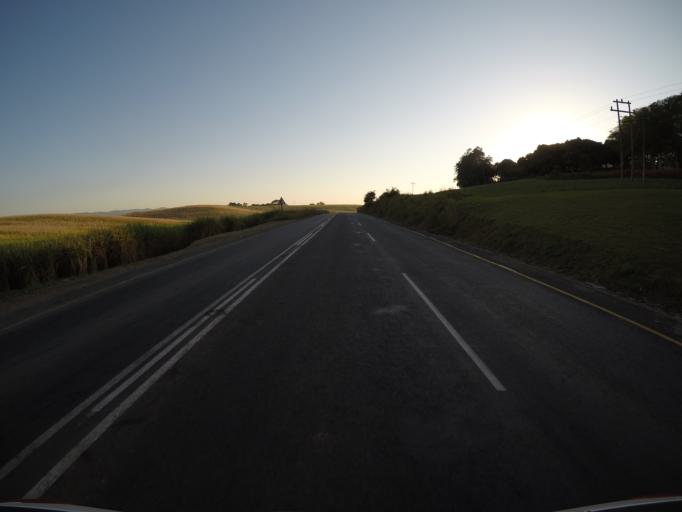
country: ZA
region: KwaZulu-Natal
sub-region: uThungulu District Municipality
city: eSikhawini
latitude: -28.9369
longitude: 31.7412
